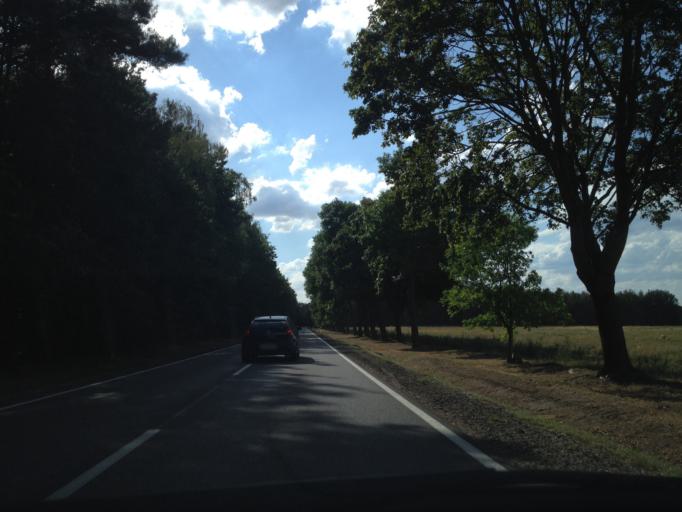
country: PL
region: Lubusz
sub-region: Powiat zarski
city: Sieniawa Zarska
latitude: 51.6304
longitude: 15.0478
